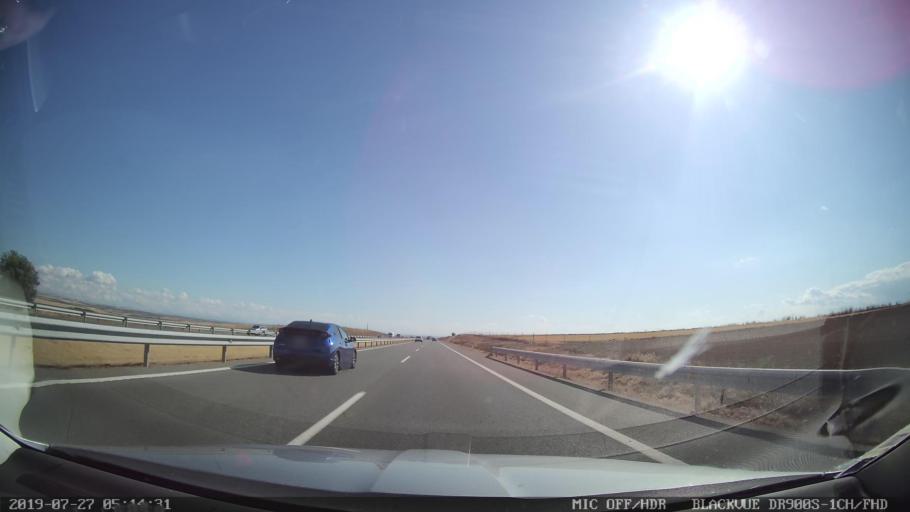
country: ES
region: Castille-La Mancha
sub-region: Province of Toledo
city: Maqueda
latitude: 40.0841
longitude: -4.3525
